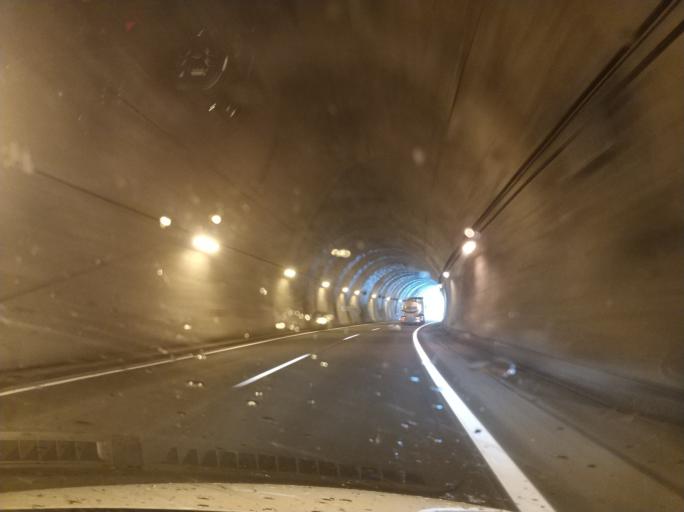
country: ES
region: Castille and Leon
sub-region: Provincia de Leon
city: Sena de Luna
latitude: 42.8859
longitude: -5.8914
